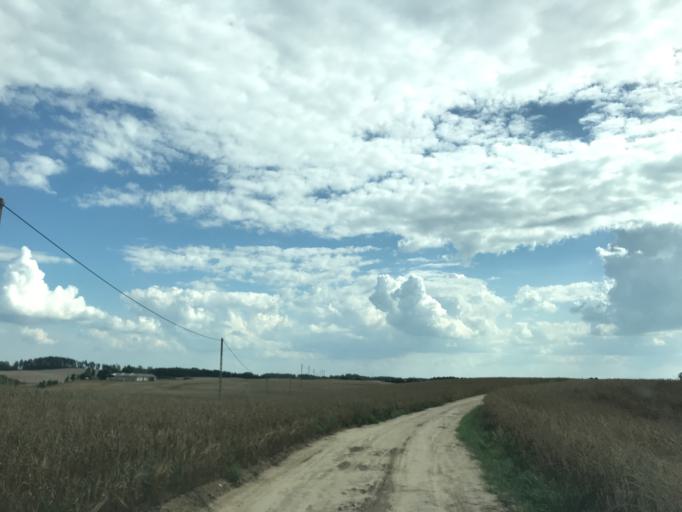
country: PL
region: Kujawsko-Pomorskie
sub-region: Powiat brodnicki
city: Brzozie
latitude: 53.3138
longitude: 19.6823
